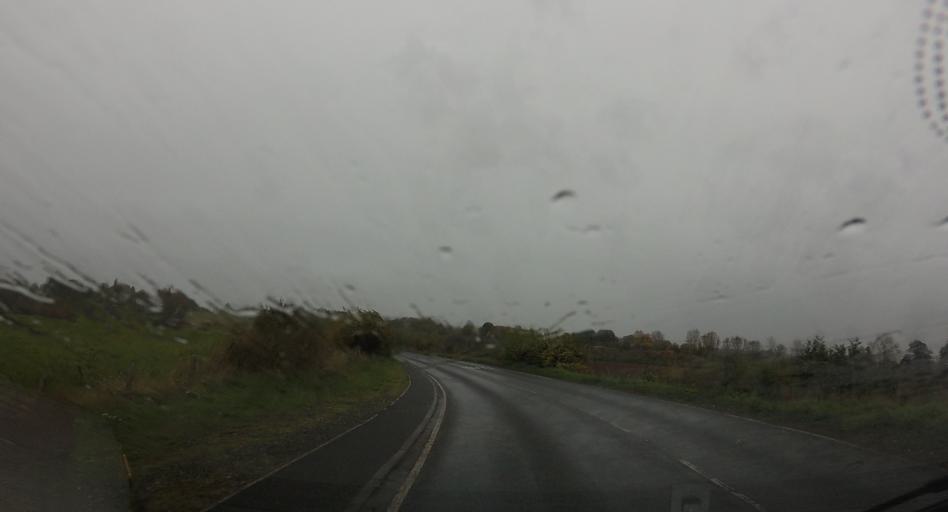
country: GB
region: Scotland
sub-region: Perth and Kinross
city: Coupar Angus
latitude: 56.5516
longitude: -3.2853
